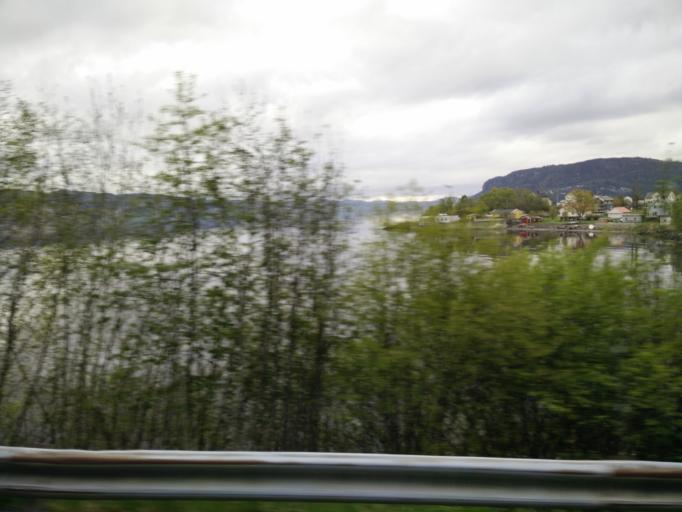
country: NO
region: Sor-Trondelag
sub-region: Skaun
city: Borsa
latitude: 63.3218
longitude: 10.1329
